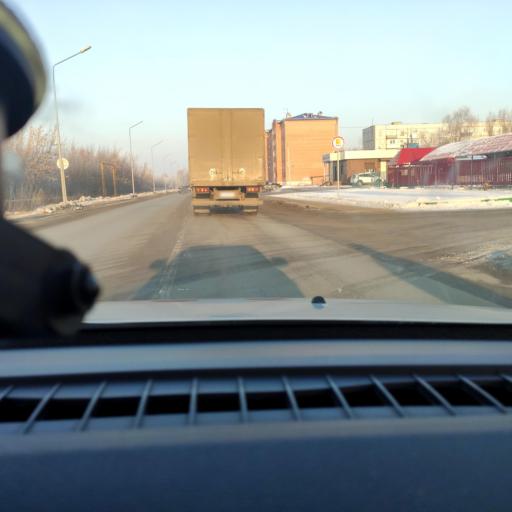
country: RU
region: Samara
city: Chapayevsk
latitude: 52.9699
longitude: 49.6977
